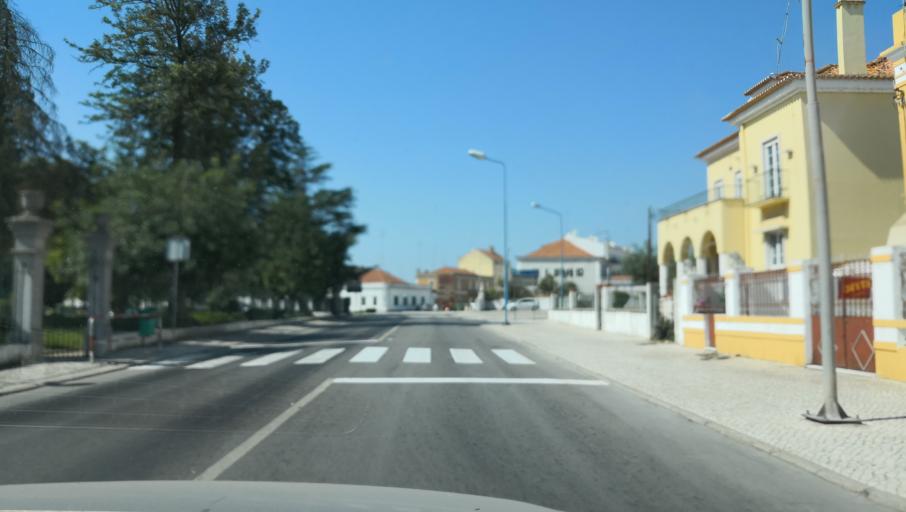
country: PT
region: Setubal
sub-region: Alcacer do Sal
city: Alcacer do Sal
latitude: 38.3697
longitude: -8.5010
